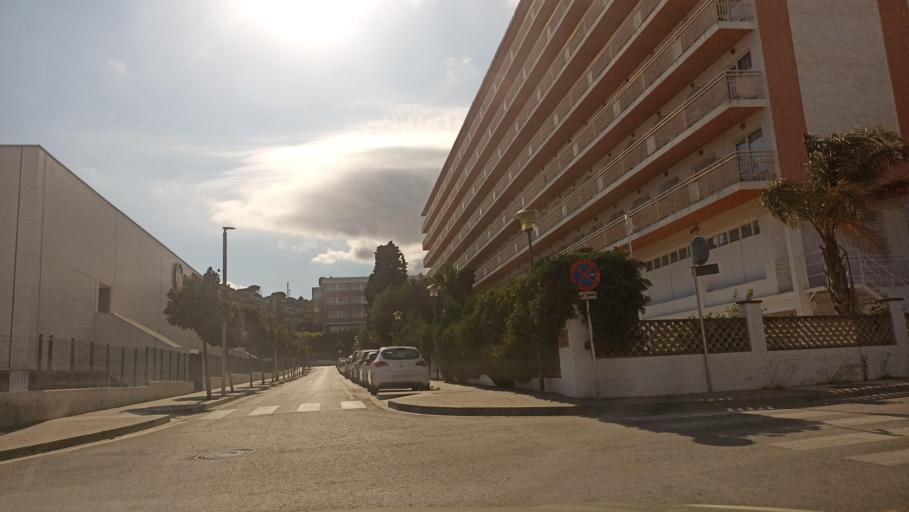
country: ES
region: Catalonia
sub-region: Provincia de Barcelona
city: Calella
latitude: 41.6151
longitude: 2.6530
